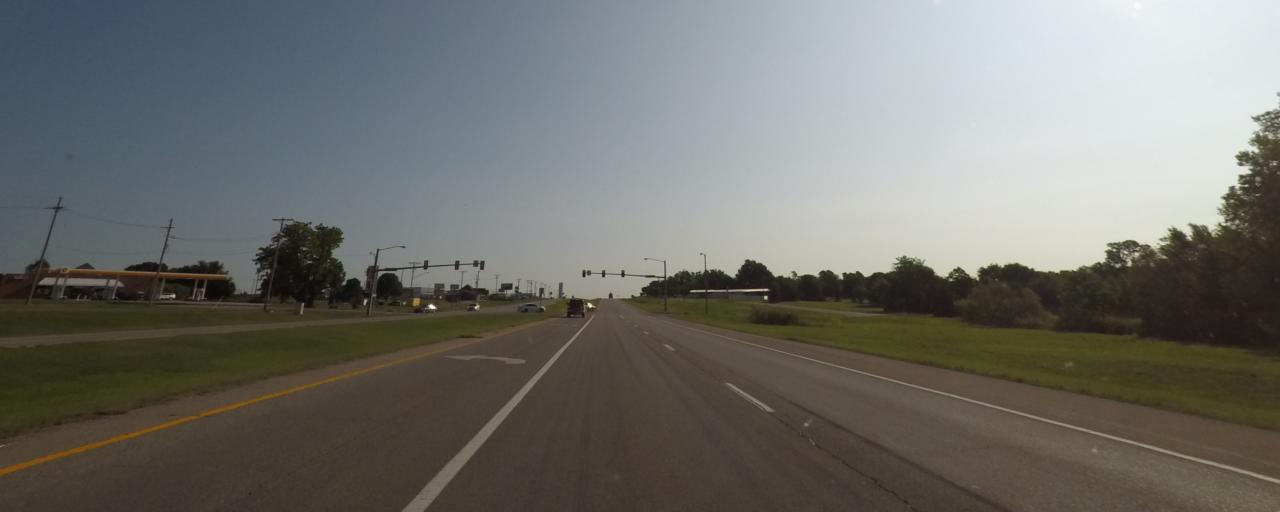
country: US
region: Oklahoma
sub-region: McClain County
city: Blanchard
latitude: 35.1448
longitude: -97.6431
